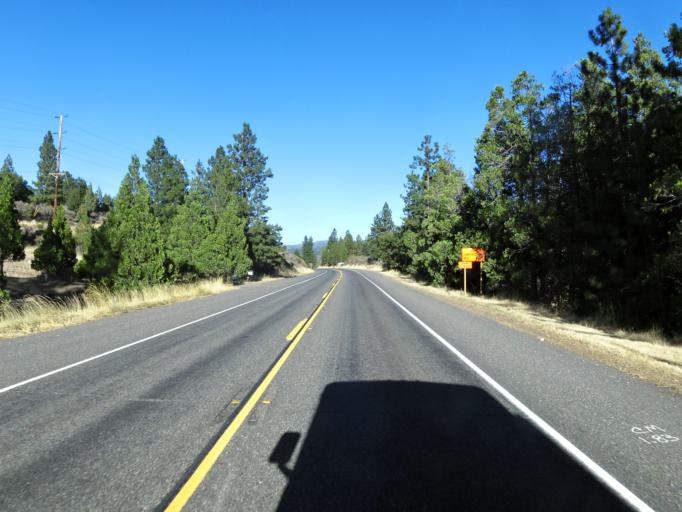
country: US
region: California
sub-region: Siskiyou County
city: Weed
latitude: 41.4425
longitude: -122.3771
